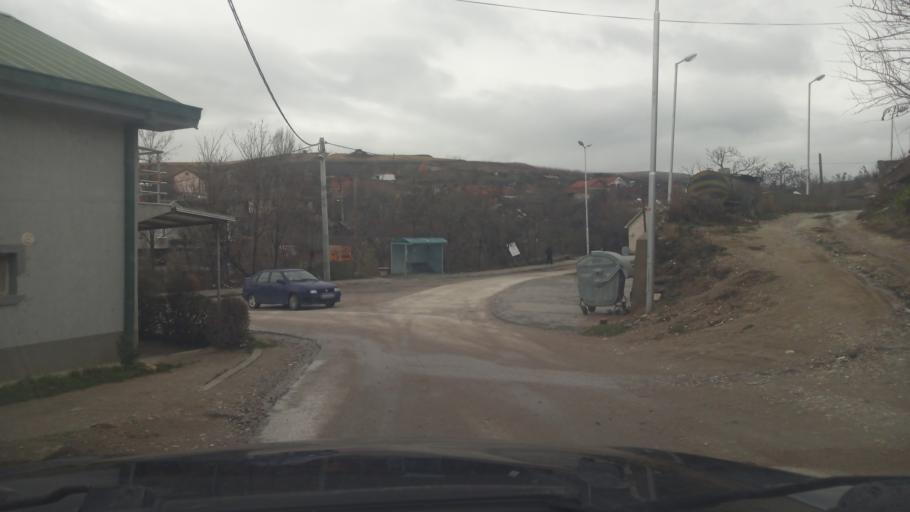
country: MK
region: Gradsko
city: Gradsko
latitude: 41.6011
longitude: 21.8984
